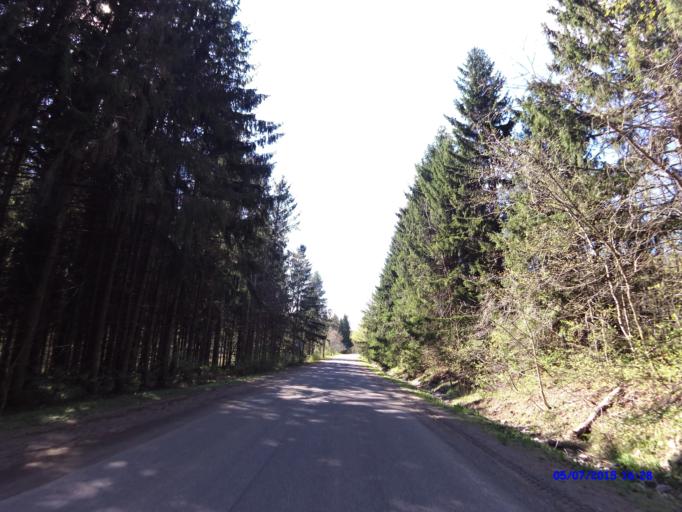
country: US
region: New York
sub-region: Cattaraugus County
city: Little Valley
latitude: 42.3139
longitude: -78.6832
